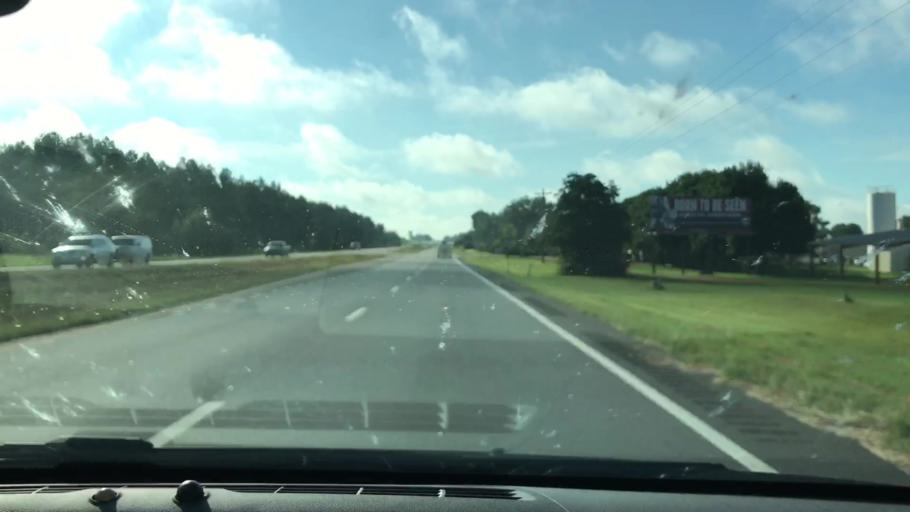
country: US
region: Georgia
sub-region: Terrell County
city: Dawson
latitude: 31.7438
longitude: -84.4156
